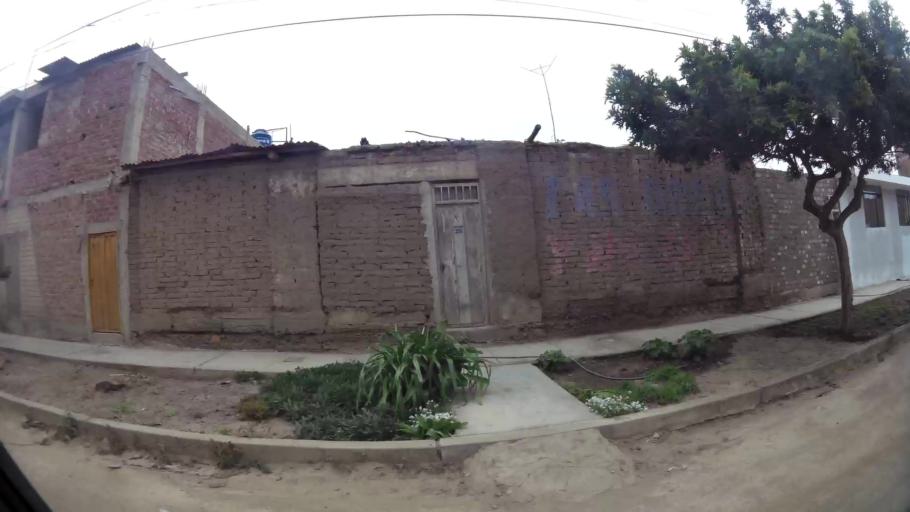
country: PE
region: La Libertad
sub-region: Provincia de Trujillo
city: Buenos Aires
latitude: -8.1431
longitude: -79.0517
